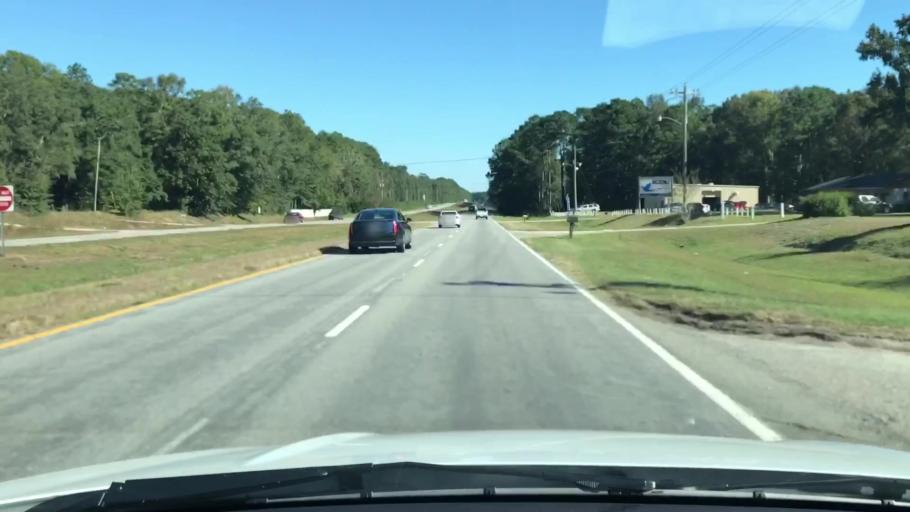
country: US
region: South Carolina
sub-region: Charleston County
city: Ravenel
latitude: 32.7830
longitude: -80.2039
